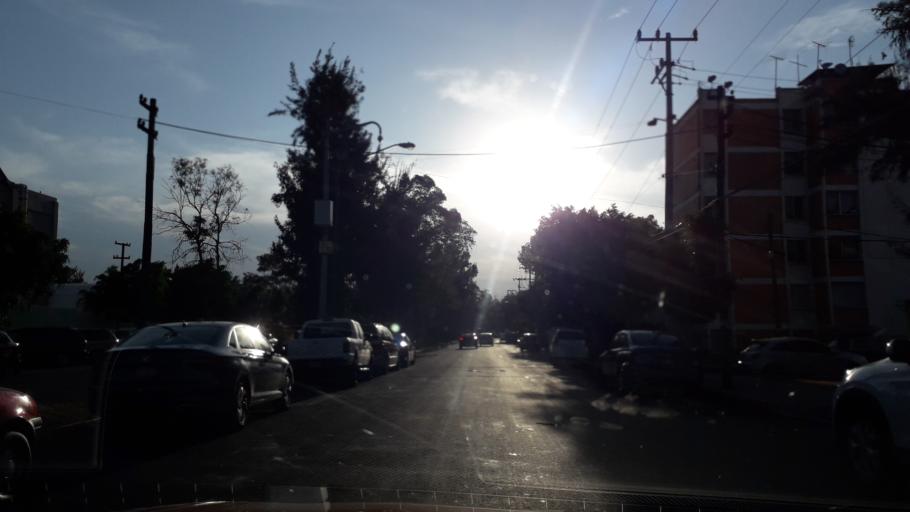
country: MX
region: Mexico City
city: Iztapalapa
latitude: 19.3585
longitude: -99.0520
